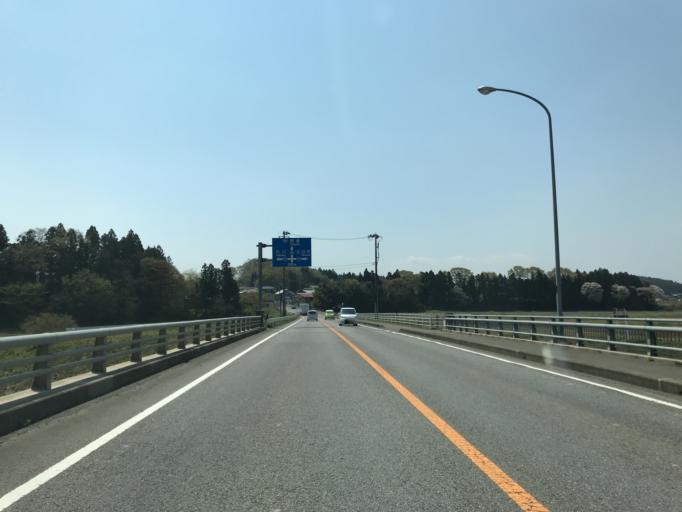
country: JP
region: Fukushima
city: Ishikawa
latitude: 37.1220
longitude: 140.3502
